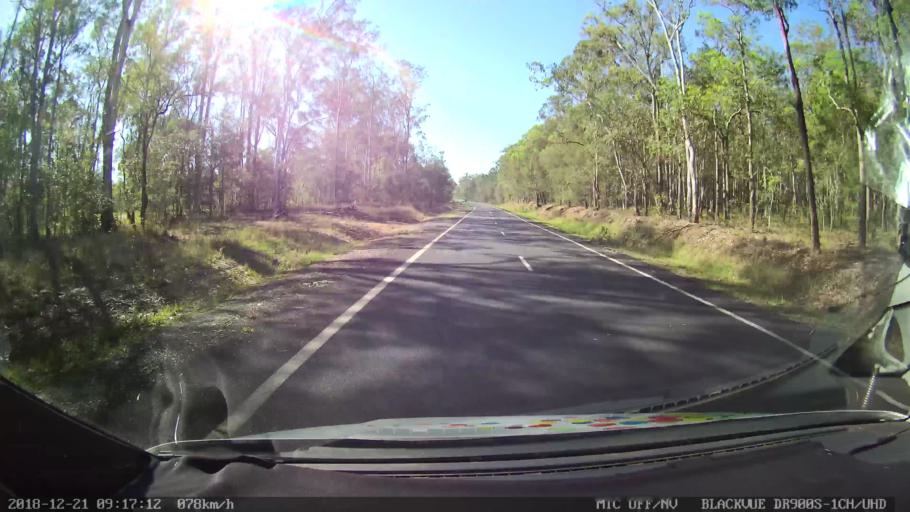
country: AU
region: New South Wales
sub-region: Clarence Valley
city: Maclean
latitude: -29.2896
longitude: 152.9897
